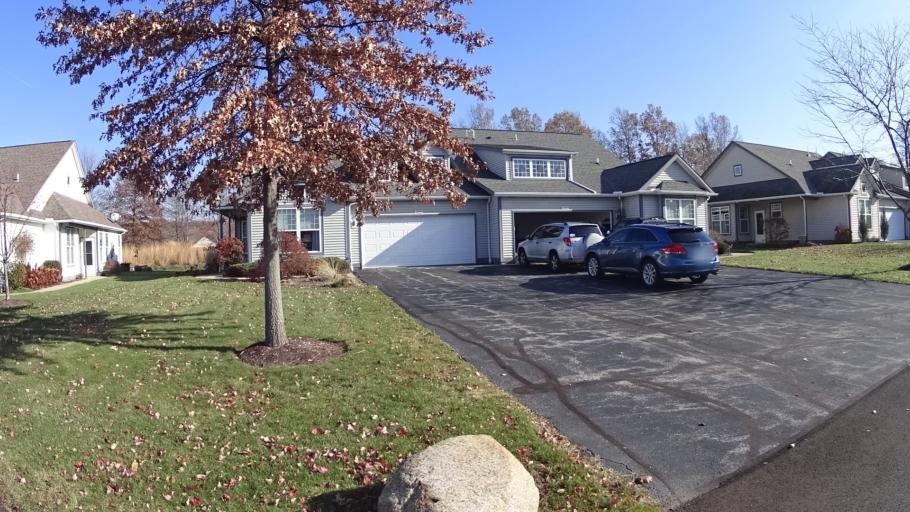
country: US
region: Ohio
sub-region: Lorain County
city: Avon Center
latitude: 41.4575
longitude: -82.0071
